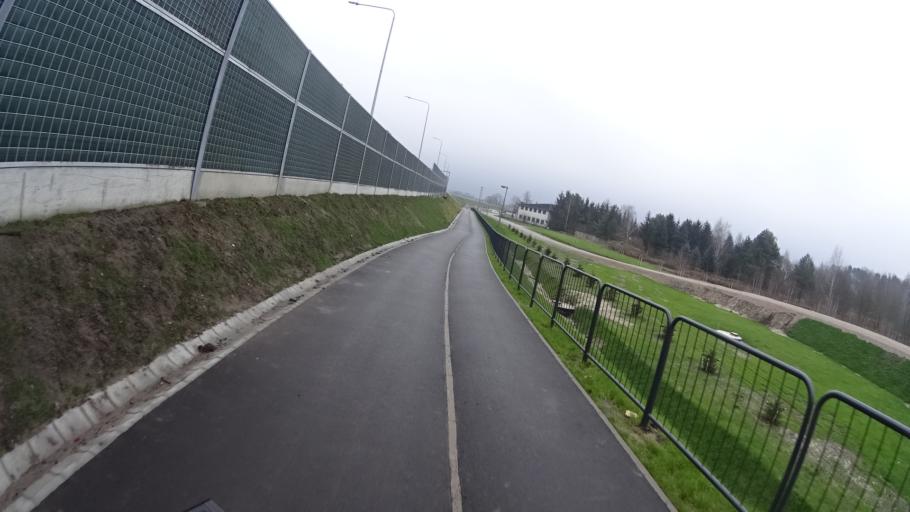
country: PL
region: Masovian Voivodeship
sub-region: Warszawa
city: Wawer
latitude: 52.1633
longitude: 21.1573
